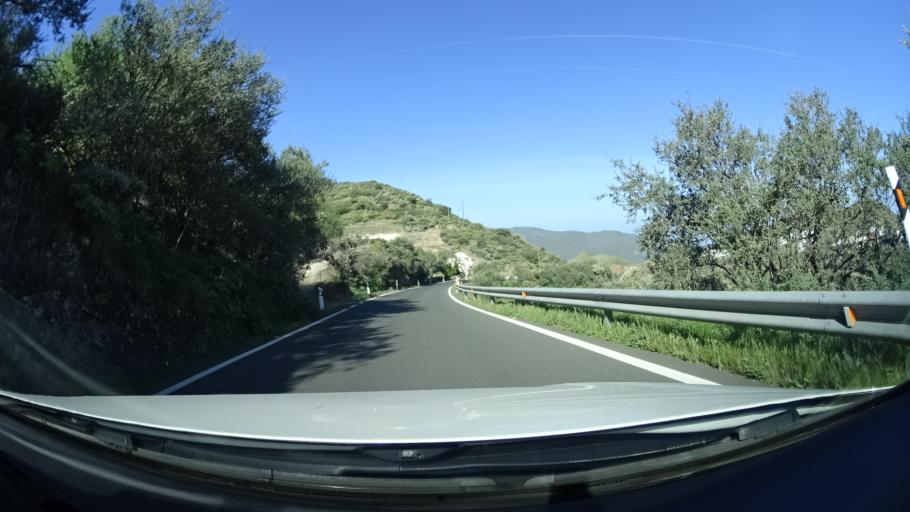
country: ES
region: Canary Islands
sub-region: Provincia de Las Palmas
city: Artenara
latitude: 28.0244
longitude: -15.6375
